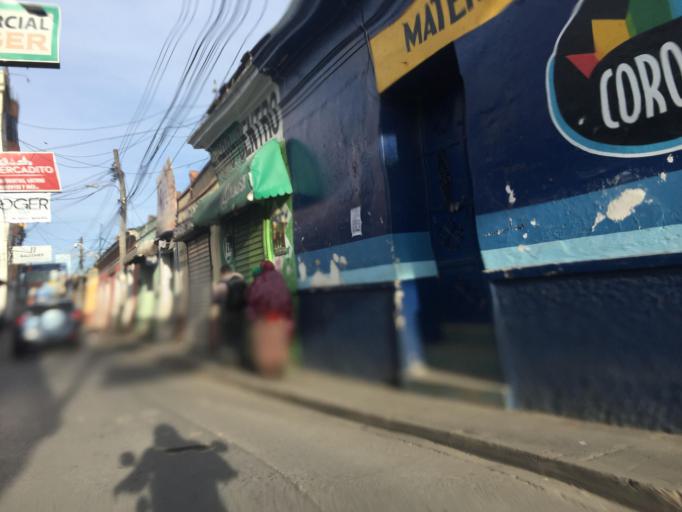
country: GT
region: Totonicapan
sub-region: Municipio de Totonicapan
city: Totonicapan
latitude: 14.9119
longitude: -91.3613
